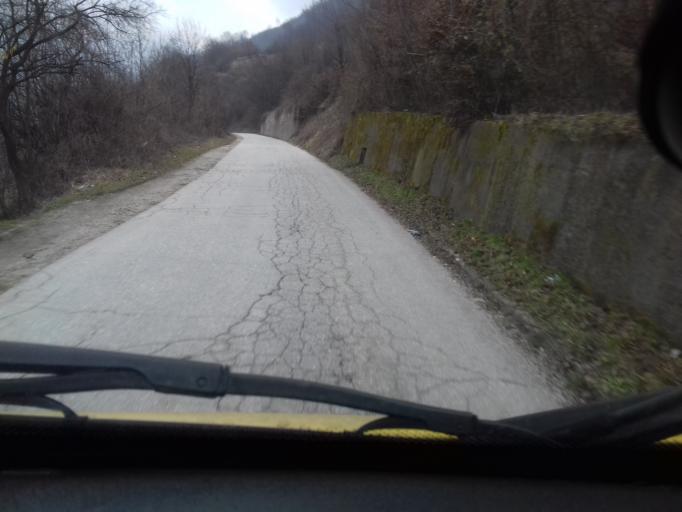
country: BA
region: Federation of Bosnia and Herzegovina
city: Zenica
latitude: 44.2424
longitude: 17.9172
